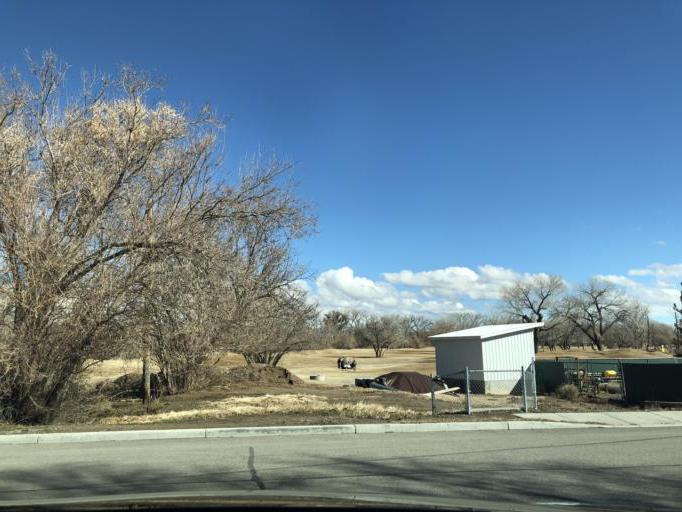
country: US
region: Utah
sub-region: Carbon County
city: East Carbon City
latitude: 38.9907
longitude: -110.1552
